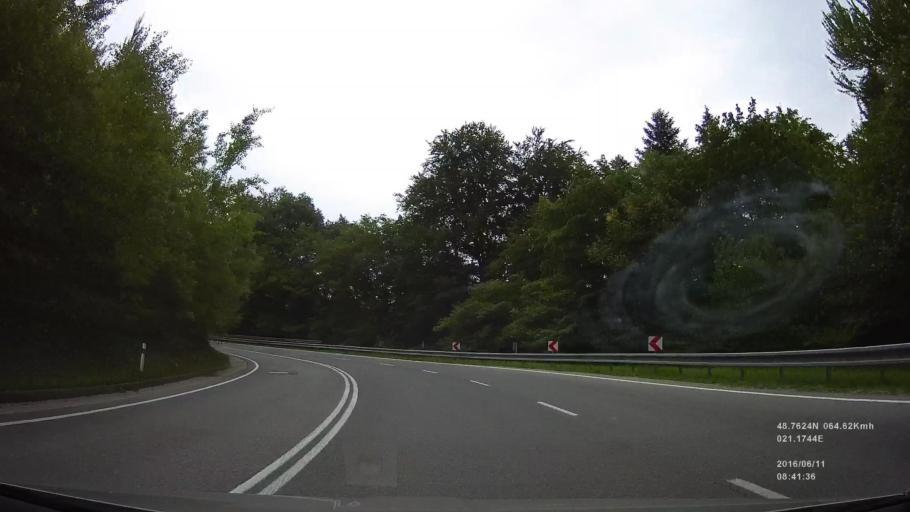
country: SK
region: Kosicky
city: Kosice
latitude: 48.7520
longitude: 21.2211
